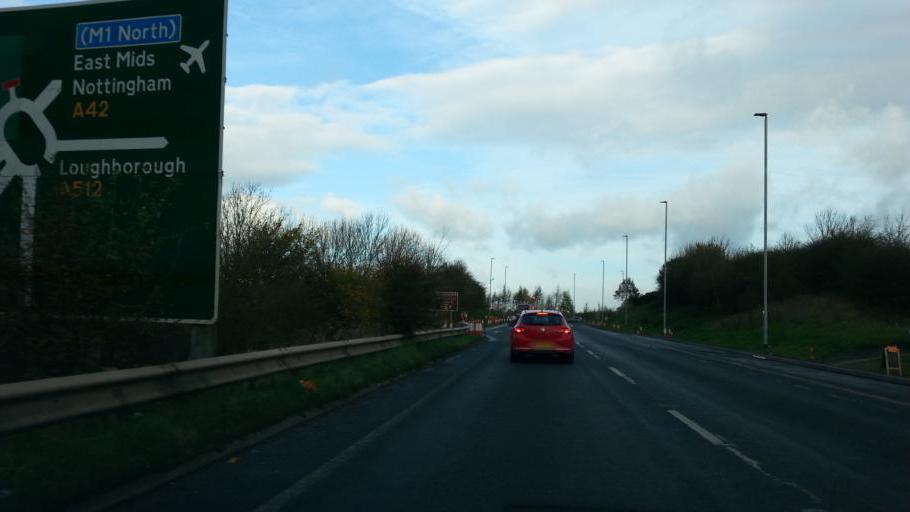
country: GB
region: England
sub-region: Leicestershire
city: Ashby de la Zouch
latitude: 52.7472
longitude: -1.4443
